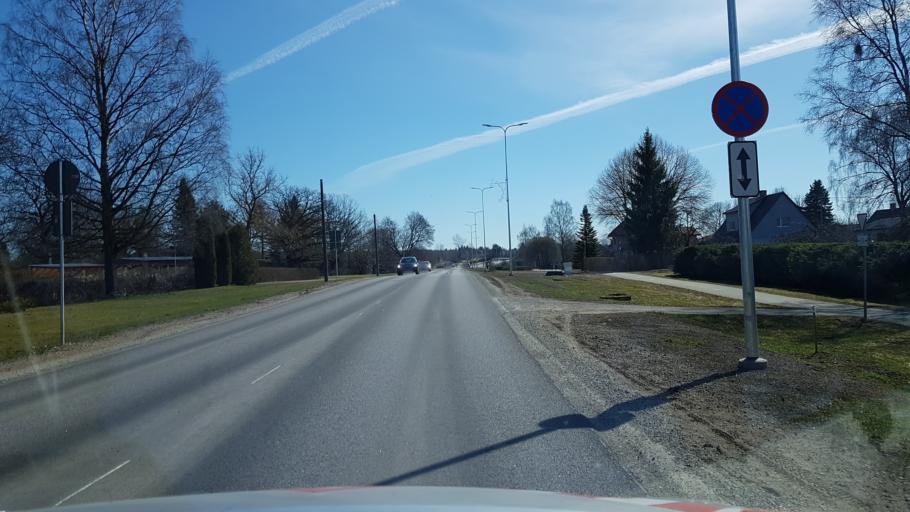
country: EE
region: Laeaene-Virumaa
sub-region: Vinni vald
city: Vinni
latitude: 59.2822
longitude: 26.4185
